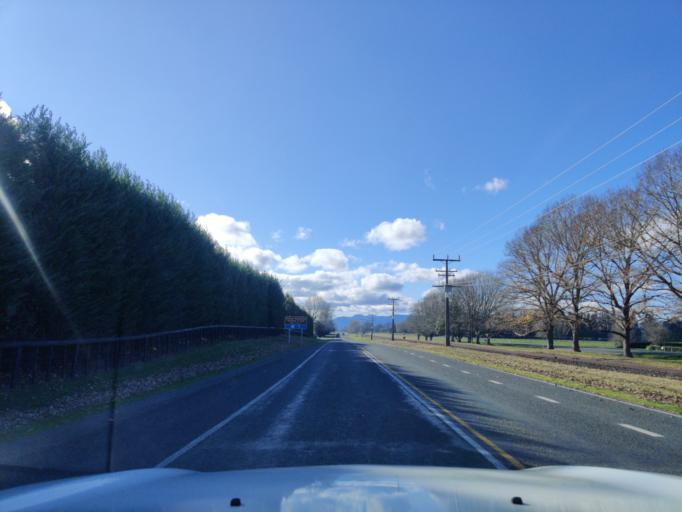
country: NZ
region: Waikato
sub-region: Matamata-Piako District
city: Matamata
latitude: -37.8525
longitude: 175.7584
